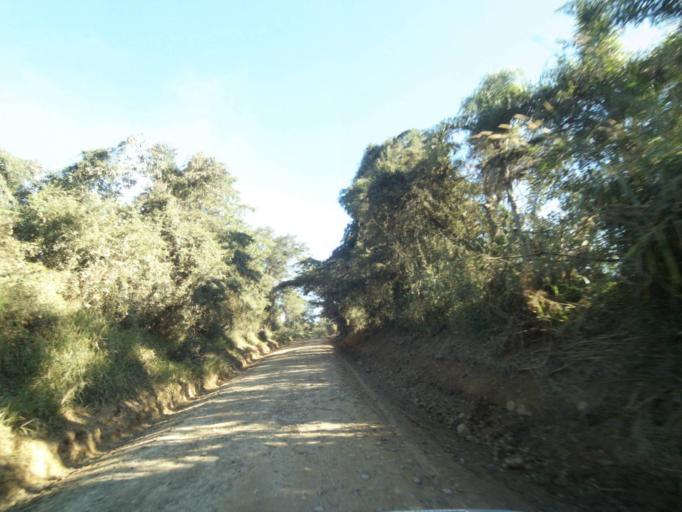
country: BR
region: Parana
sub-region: Tibagi
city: Tibagi
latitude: -24.5311
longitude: -50.5150
